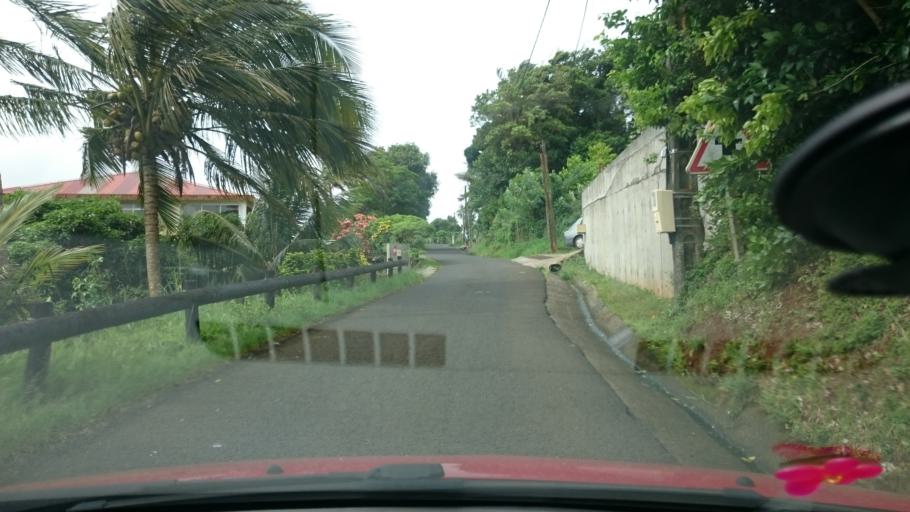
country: MQ
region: Martinique
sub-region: Martinique
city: Riviere-Pilote
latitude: 14.4961
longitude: -60.9207
